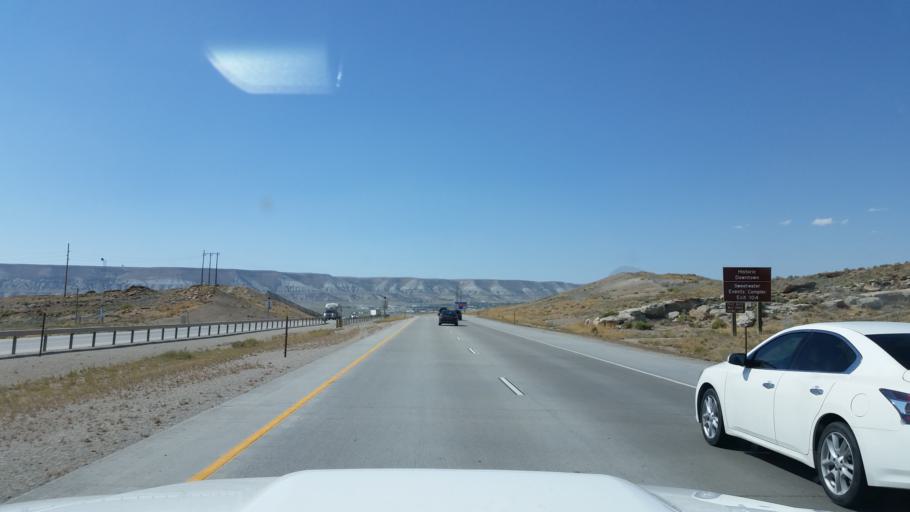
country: US
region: Wyoming
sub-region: Sweetwater County
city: Rock Springs
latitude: 41.6079
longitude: -109.2116
